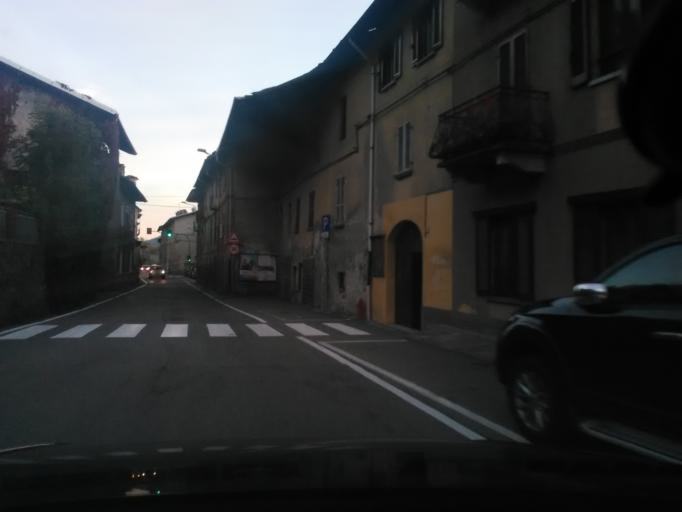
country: IT
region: Piedmont
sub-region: Provincia di Vercelli
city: Serravalle Sesia
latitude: 45.7064
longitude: 8.2999
